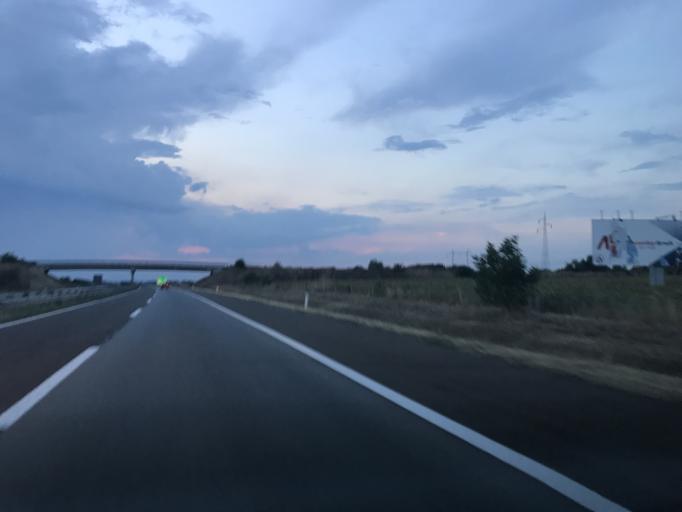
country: RS
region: Central Serbia
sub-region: Pomoravski Okrug
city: Cuprija
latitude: 43.9417
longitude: 21.3863
